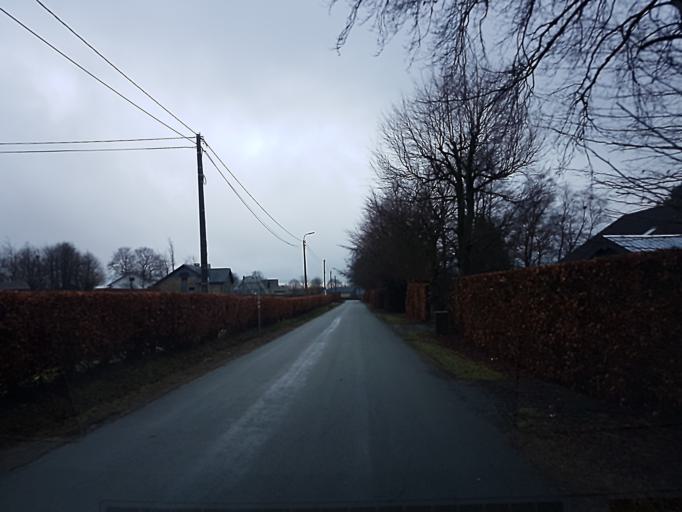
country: BE
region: Wallonia
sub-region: Province de Liege
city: Waimes
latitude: 50.4728
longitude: 6.1096
